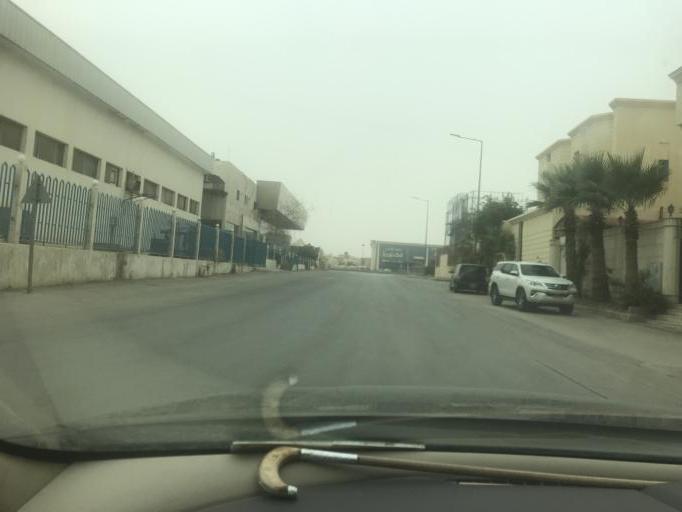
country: SA
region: Ar Riyad
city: Riyadh
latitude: 24.7282
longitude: 46.7865
